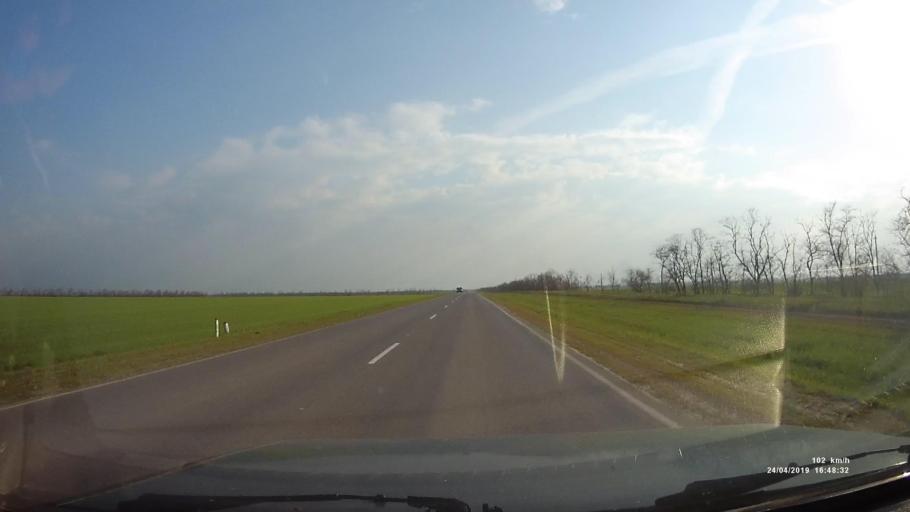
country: RU
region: Rostov
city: Proletarsk
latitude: 46.7296
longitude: 41.7742
